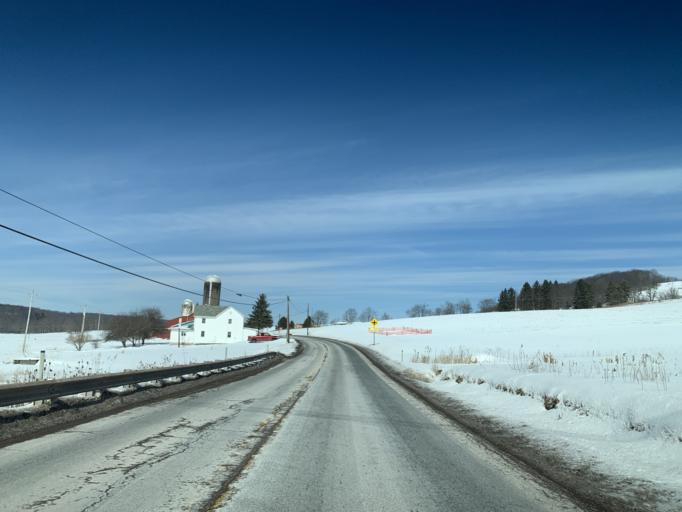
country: US
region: West Virginia
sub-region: Preston County
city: Terra Alta
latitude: 39.7089
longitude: -79.4446
